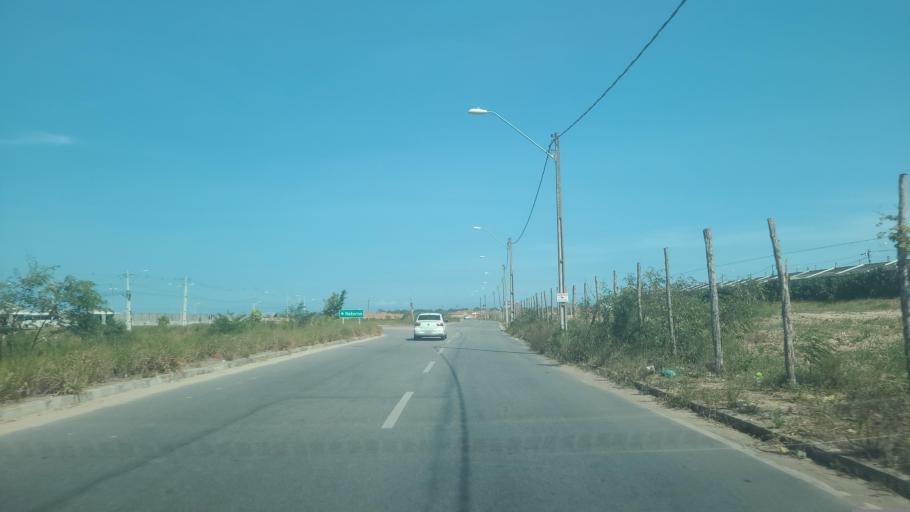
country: BR
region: Alagoas
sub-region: Satuba
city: Satuba
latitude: -9.5318
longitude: -35.7713
